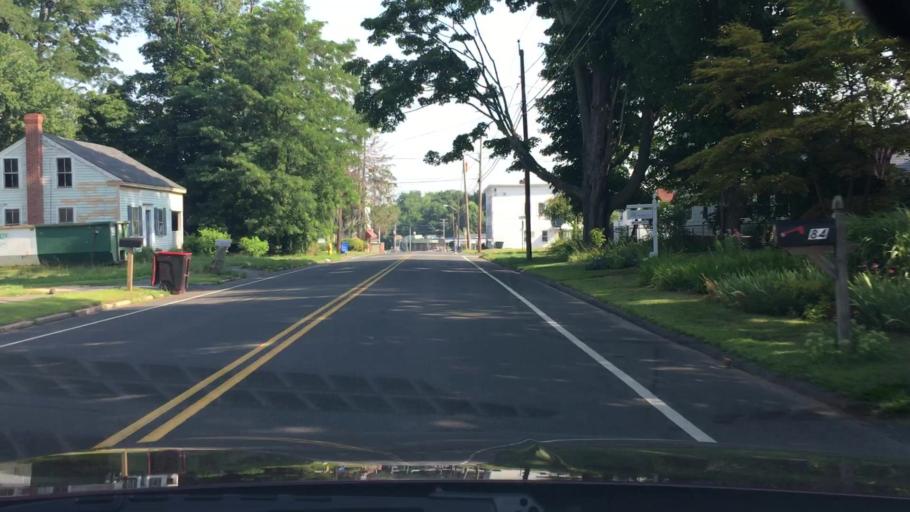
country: US
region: Massachusetts
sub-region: Hampden County
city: East Longmeadow
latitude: 42.0629
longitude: -72.5126
